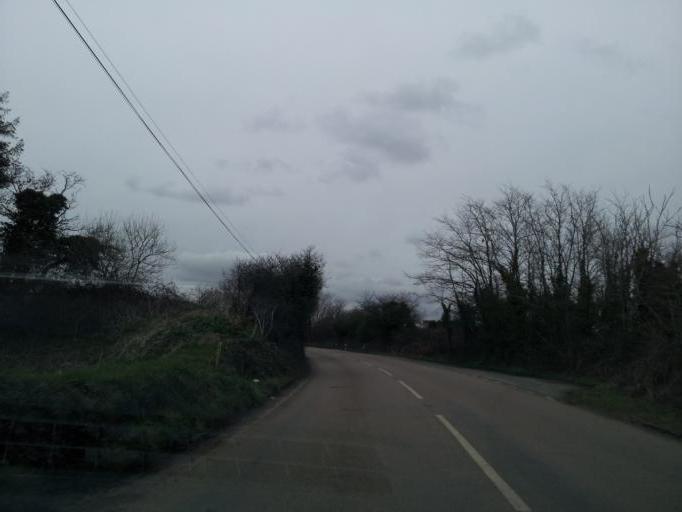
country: GB
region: England
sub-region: Cornwall
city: Redruth
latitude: 50.2594
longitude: -5.2552
